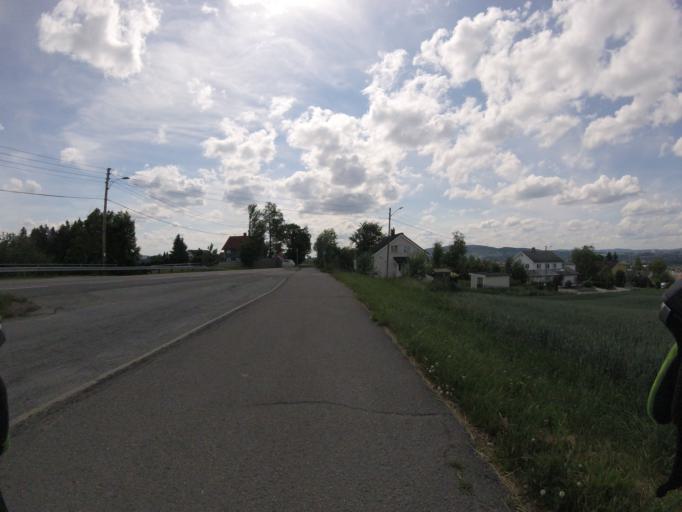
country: NO
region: Akershus
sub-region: Skedsmo
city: Lillestrom
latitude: 59.9778
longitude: 11.0560
